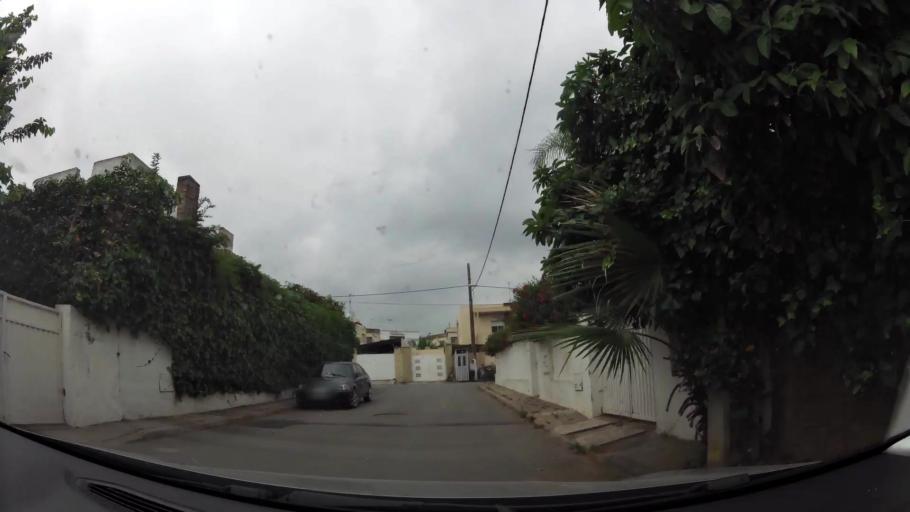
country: MA
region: Rabat-Sale-Zemmour-Zaer
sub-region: Rabat
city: Rabat
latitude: 33.9867
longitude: -6.8266
